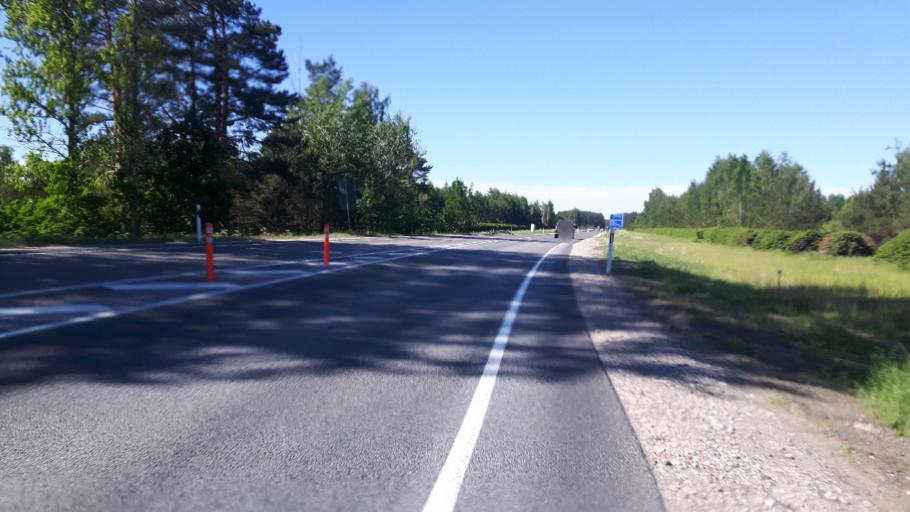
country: EE
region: Paernumaa
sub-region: Paikuse vald
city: Paikuse
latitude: 58.2948
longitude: 24.6053
